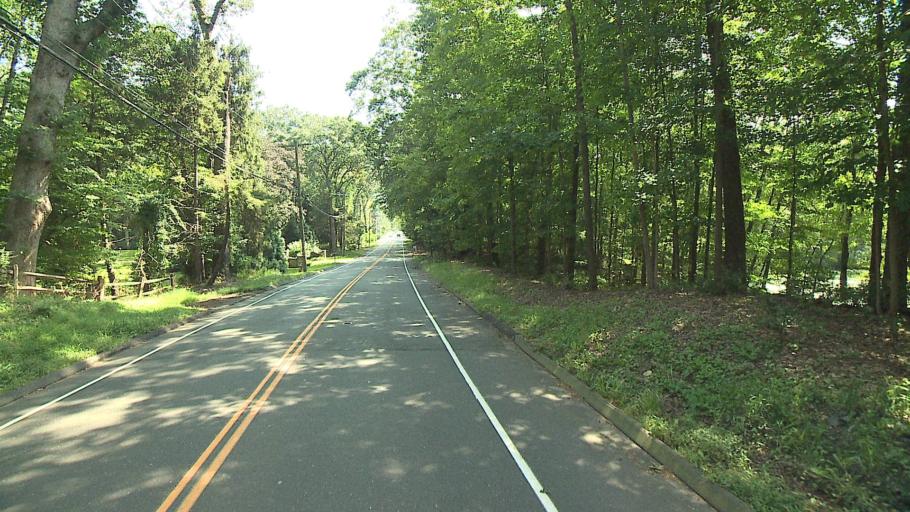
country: US
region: Connecticut
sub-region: Fairfield County
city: Westport
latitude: 41.1780
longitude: -73.3638
